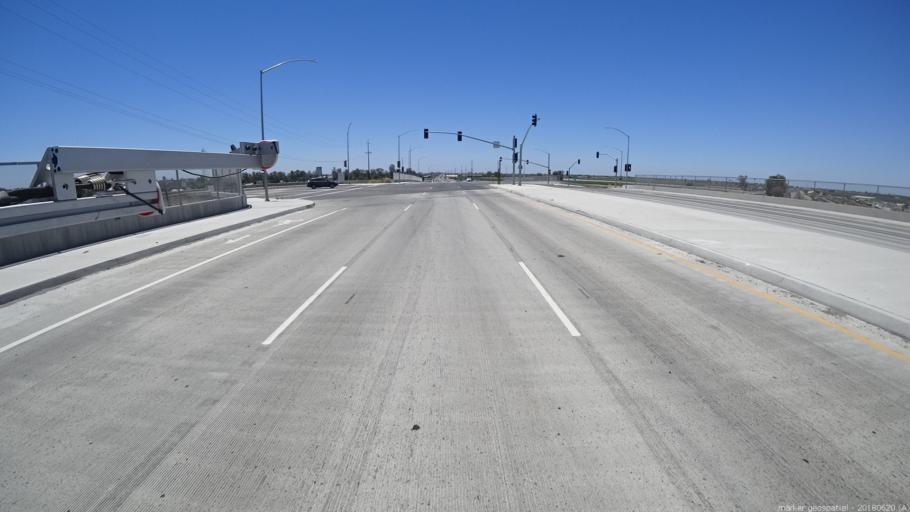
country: US
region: California
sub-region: Madera County
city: Parksdale
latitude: 36.9237
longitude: -120.0204
